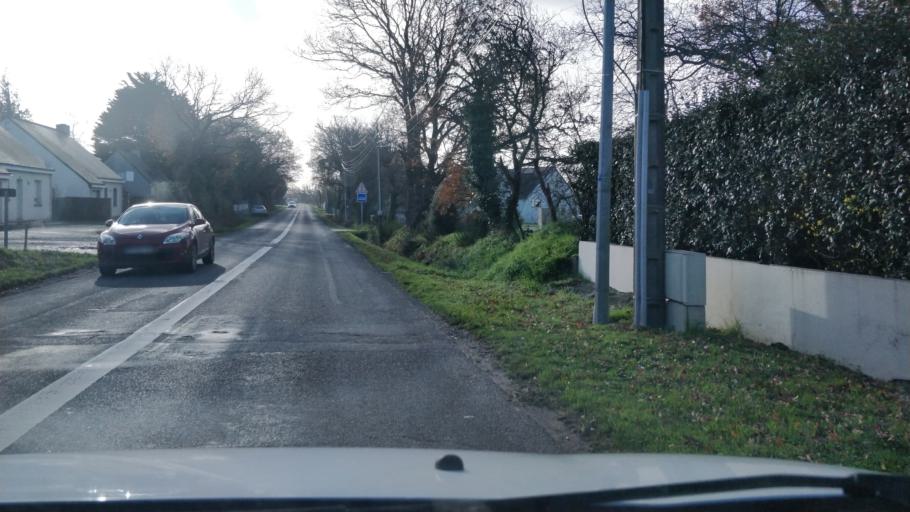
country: FR
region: Pays de la Loire
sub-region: Departement de la Loire-Atlantique
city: Guerande
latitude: 47.3543
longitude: -2.4329
